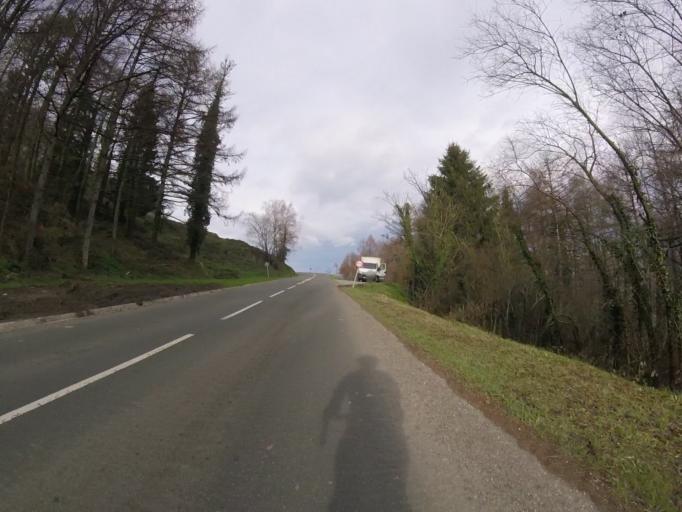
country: ES
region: Basque Country
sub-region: Provincia de Guipuzcoa
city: Errezil
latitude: 43.1469
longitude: -2.1788
